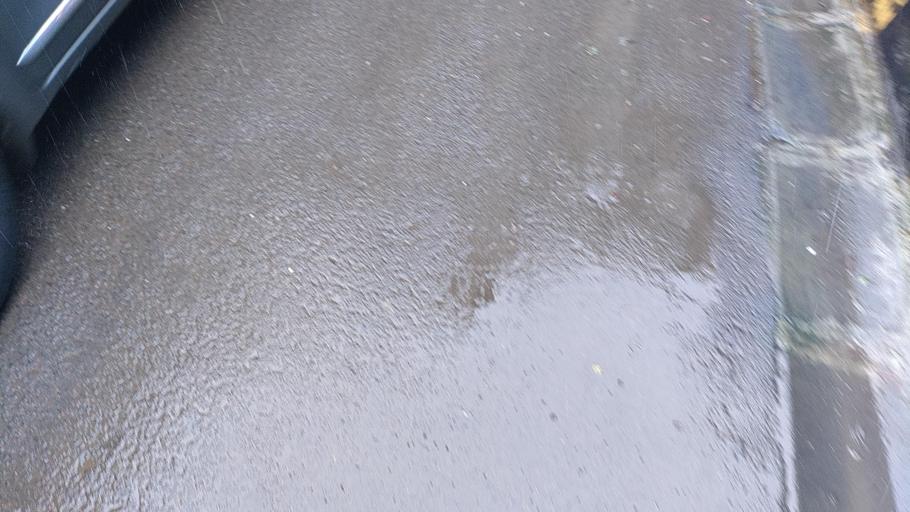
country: IN
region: Maharashtra
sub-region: Mumbai Suburban
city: Borivli
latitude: 19.2362
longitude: 72.8565
